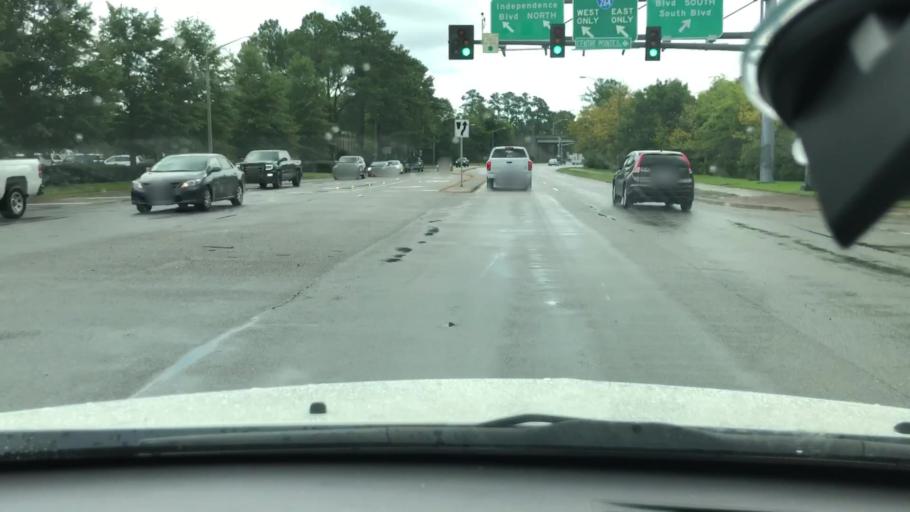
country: US
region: Virginia
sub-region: City of Chesapeake
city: Chesapeake
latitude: 36.8295
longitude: -76.1401
